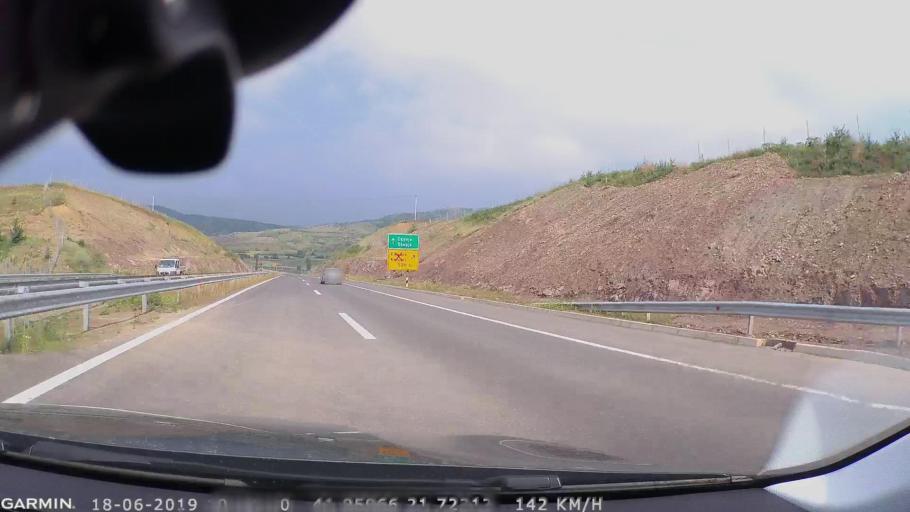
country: MK
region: Sveti Nikole
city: Gorobinci
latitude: 41.9330
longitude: 21.8261
